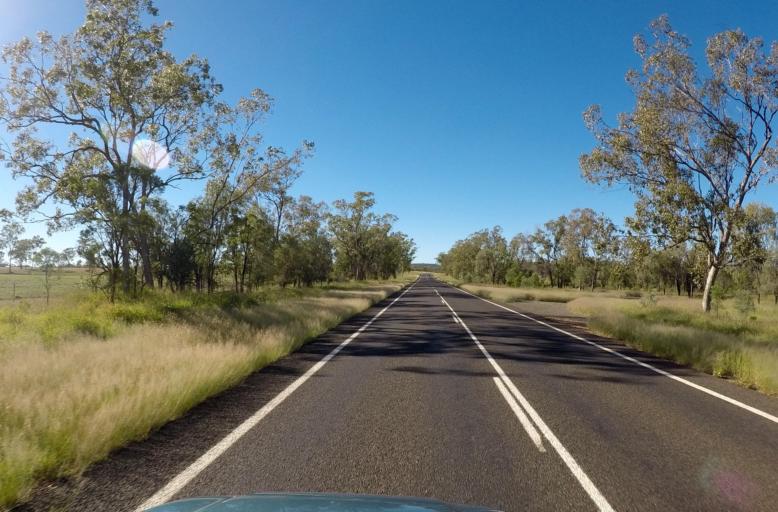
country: AU
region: Queensland
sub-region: Maranoa
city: Roma
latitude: -26.1069
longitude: 148.6505
